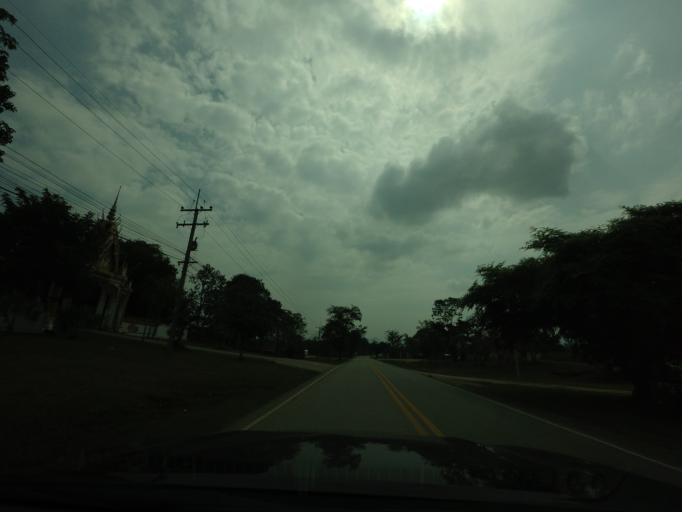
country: TH
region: Loei
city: Tha Li
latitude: 17.6438
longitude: 101.4058
